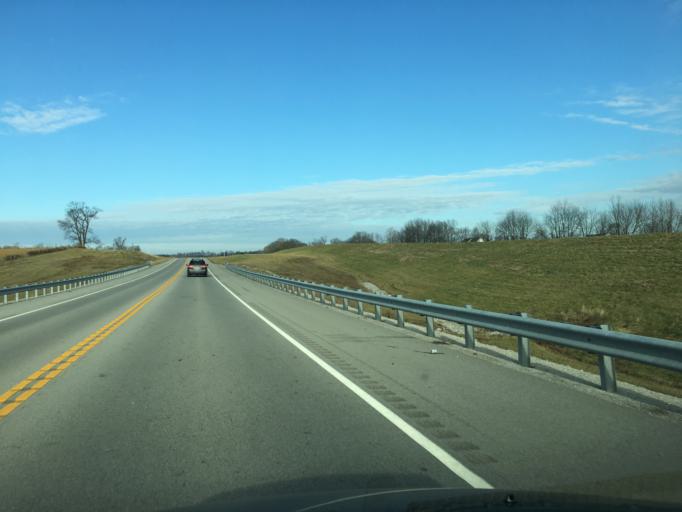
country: US
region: Kentucky
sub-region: Scott County
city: Georgetown
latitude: 38.2352
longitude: -84.5867
